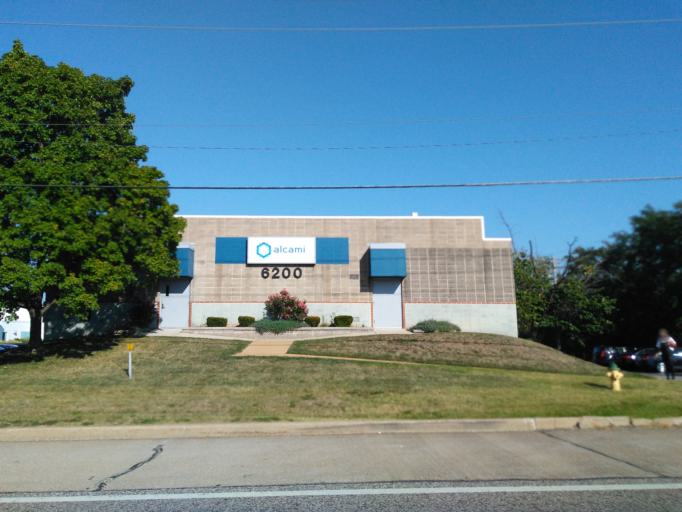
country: US
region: Missouri
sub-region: Saint Louis County
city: Green Park
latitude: 38.5167
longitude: -90.3429
